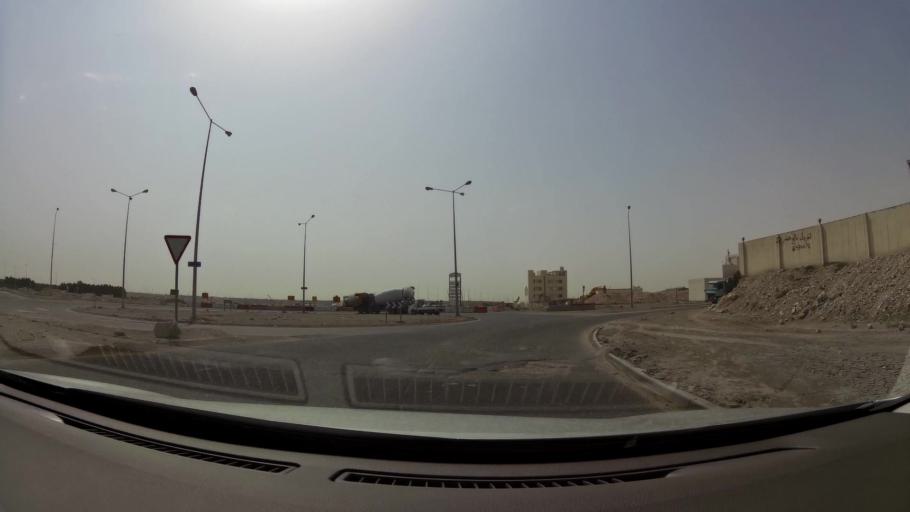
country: QA
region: Al Wakrah
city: Al Wukayr
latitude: 25.1730
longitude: 51.4690
